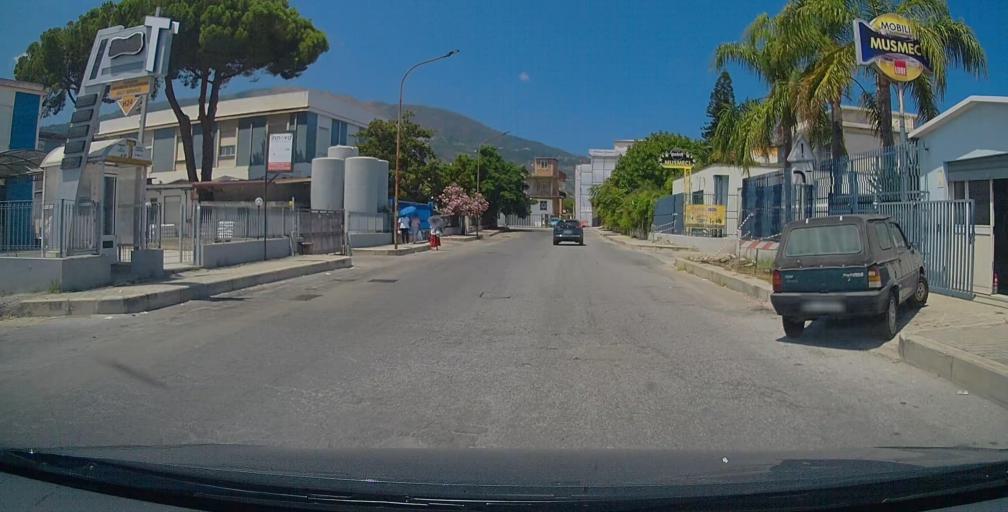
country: IT
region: Sicily
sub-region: Messina
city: Patti
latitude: 38.1495
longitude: 14.9778
